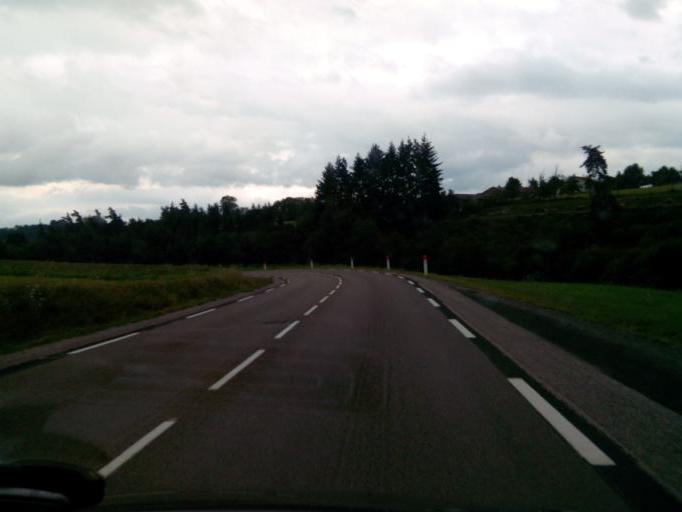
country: FR
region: Auvergne
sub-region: Departement de la Haute-Loire
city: Craponne-sur-Arzon
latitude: 45.3453
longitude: 3.8889
